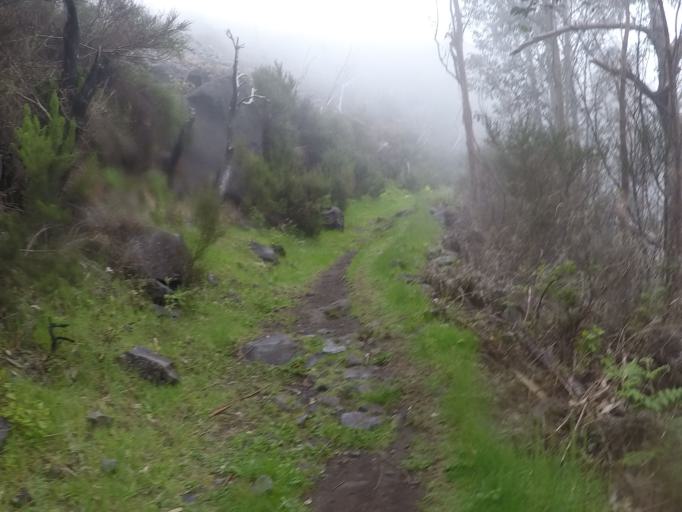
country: PT
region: Madeira
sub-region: Camara de Lobos
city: Curral das Freiras
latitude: 32.7247
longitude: -16.9853
